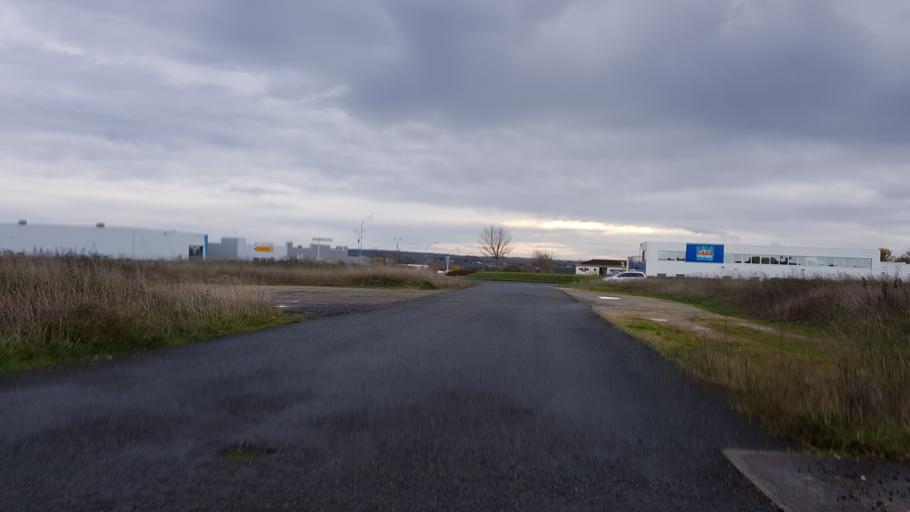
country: FR
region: Poitou-Charentes
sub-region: Departement de la Vienne
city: Chasseneuil-du-Poitou
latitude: 46.6541
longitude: 0.3607
